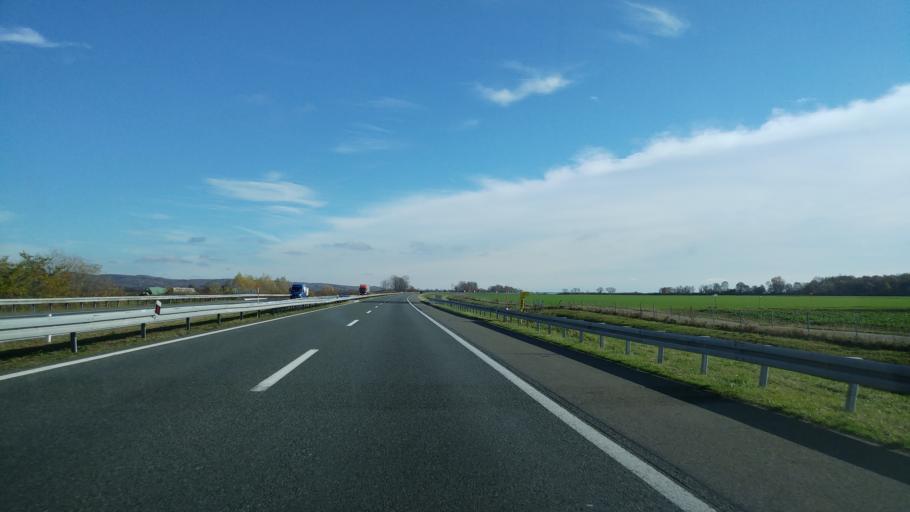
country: HR
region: Brodsko-Posavska
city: Okucani
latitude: 45.2901
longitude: 17.0918
